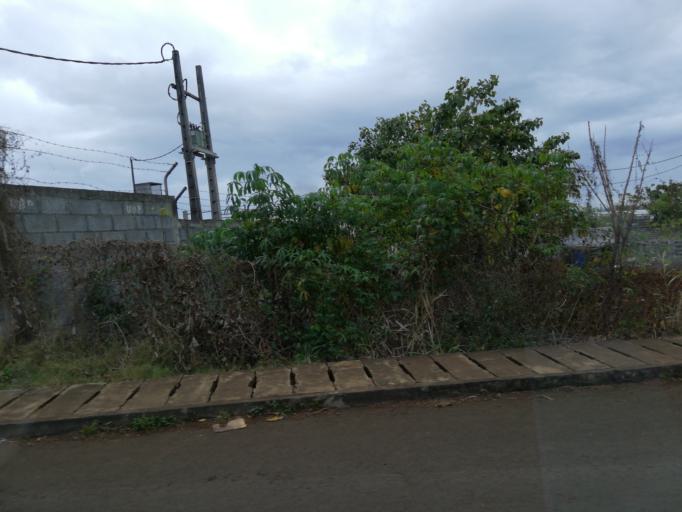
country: MU
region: Black River
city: Petite Riviere
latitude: -20.2139
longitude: 57.4646
